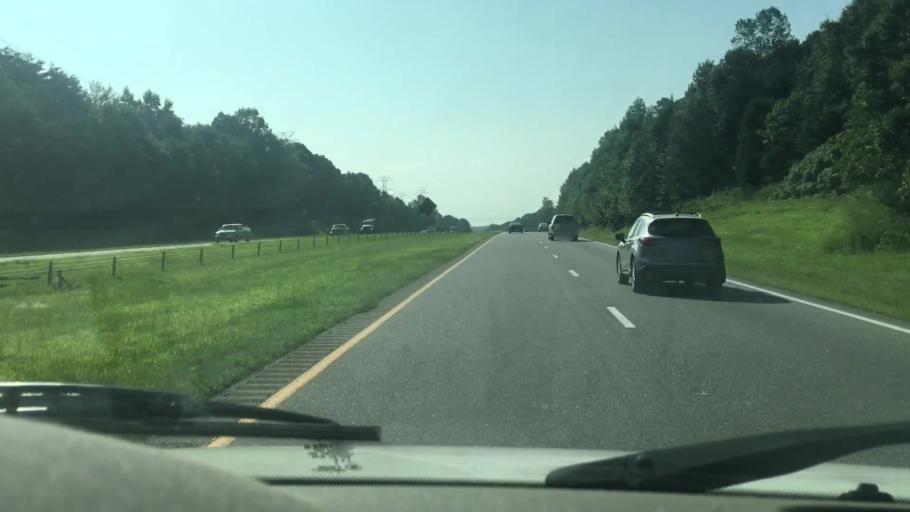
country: US
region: North Carolina
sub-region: Lincoln County
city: Lowesville
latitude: 35.3644
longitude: -80.9891
